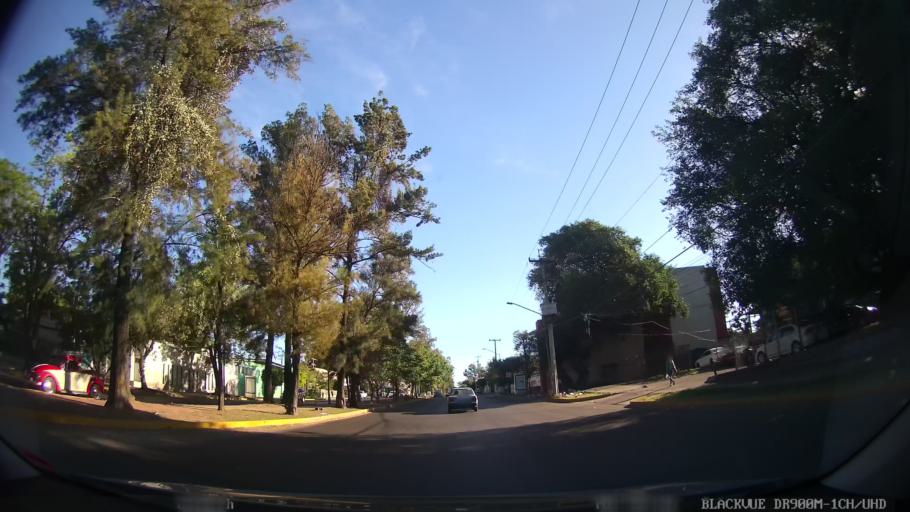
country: MX
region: Jalisco
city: Tlaquepaque
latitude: 20.6830
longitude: -103.2946
